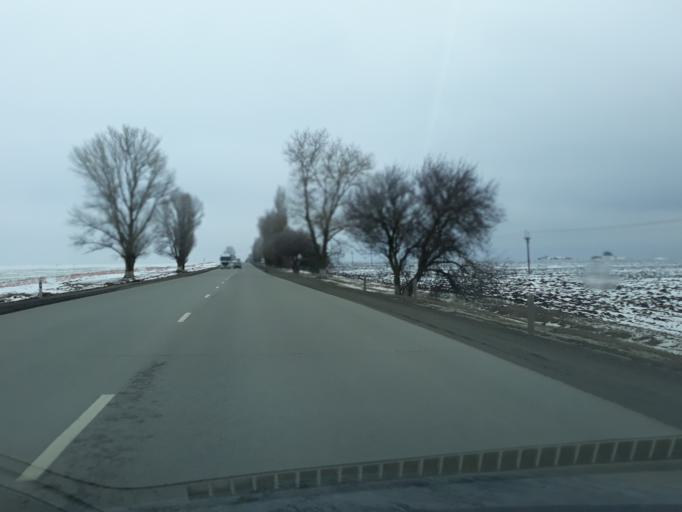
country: RU
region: Rostov
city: Primorka
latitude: 47.3039
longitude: 39.1640
